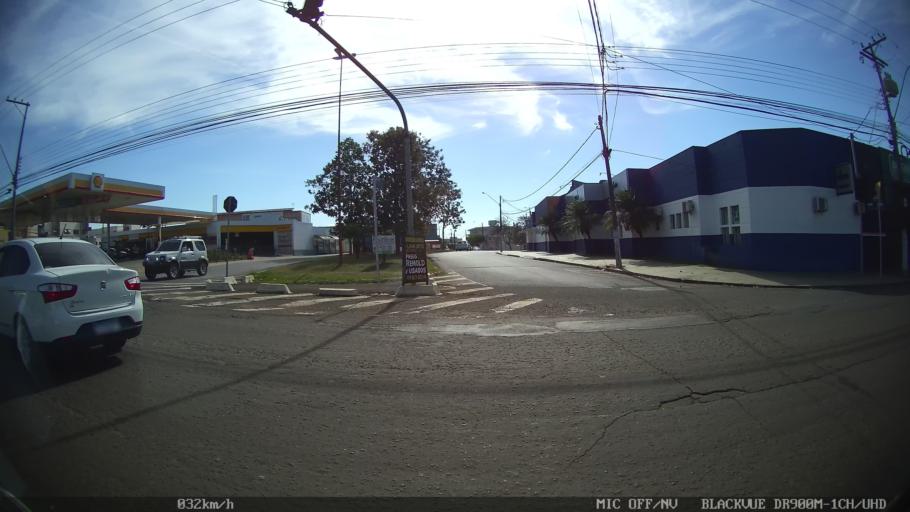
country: BR
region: Sao Paulo
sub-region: Franca
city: Franca
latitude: -20.5426
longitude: -47.4221
